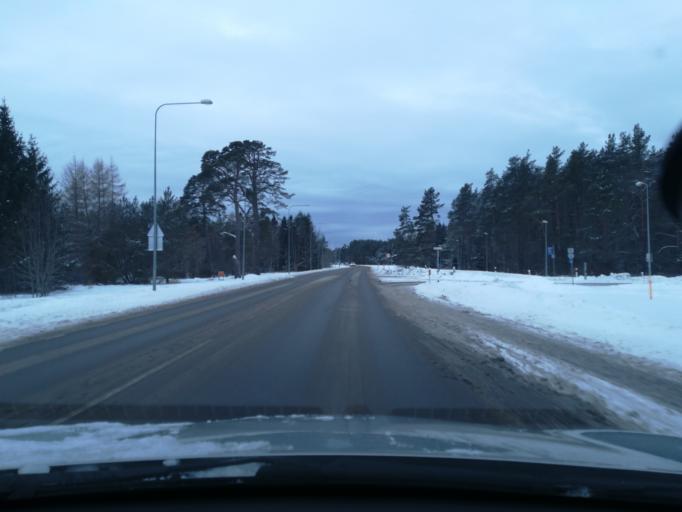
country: EE
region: Harju
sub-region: Harku vald
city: Tabasalu
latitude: 59.4371
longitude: 24.5129
